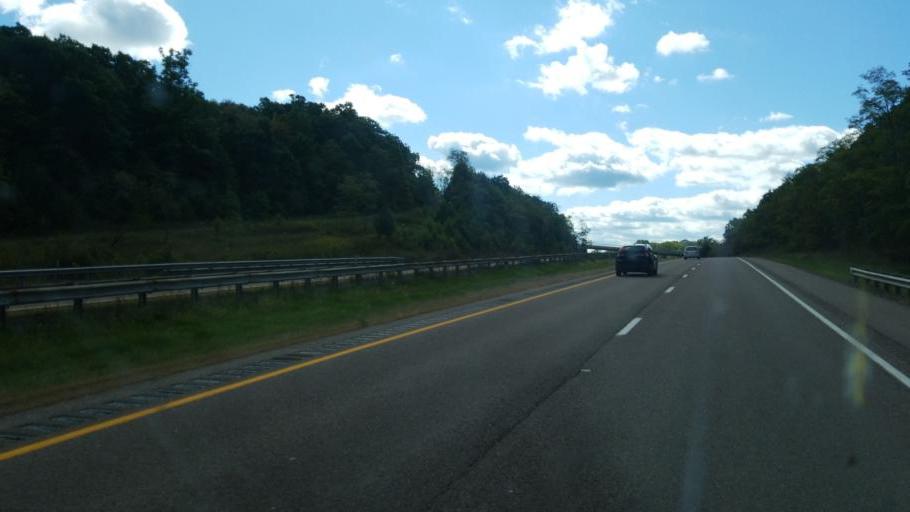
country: US
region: Maryland
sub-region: Garrett County
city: Oakland
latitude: 39.6963
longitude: -79.3362
